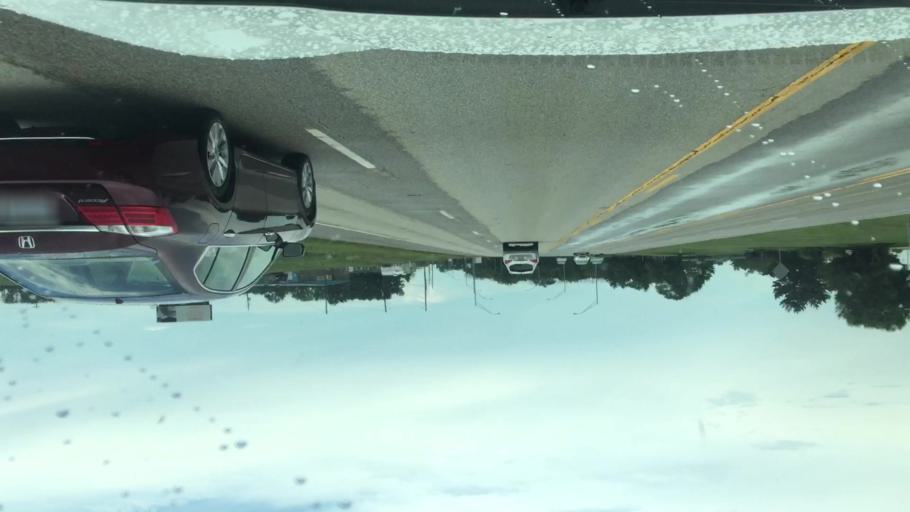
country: US
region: Ohio
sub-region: Champaign County
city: North Lewisburg
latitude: 40.2749
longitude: -83.5114
